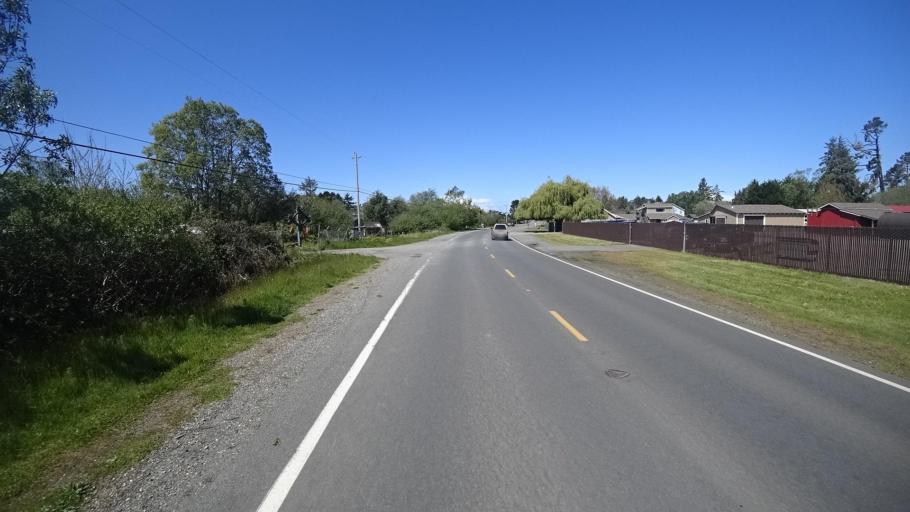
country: US
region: California
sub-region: Humboldt County
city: McKinleyville
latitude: 40.9561
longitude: -124.0950
